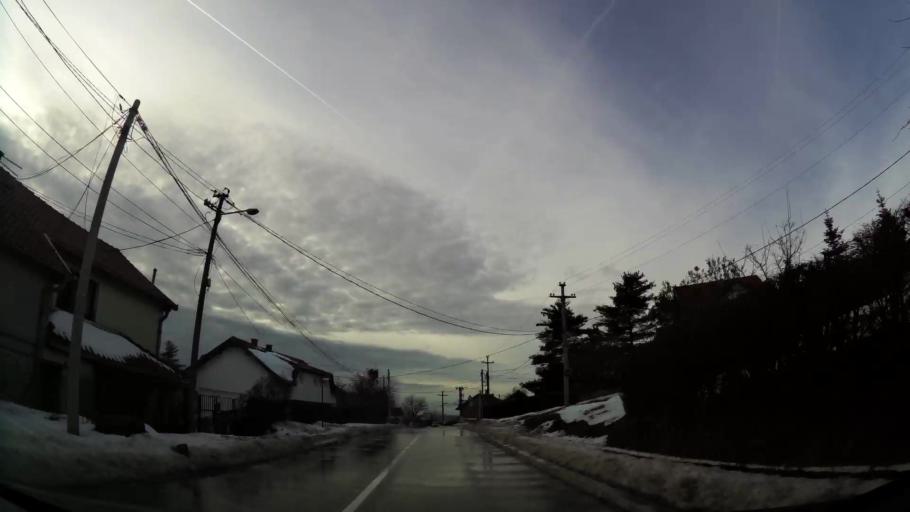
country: RS
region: Central Serbia
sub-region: Belgrade
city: Zvezdara
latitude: 44.7392
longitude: 20.5115
